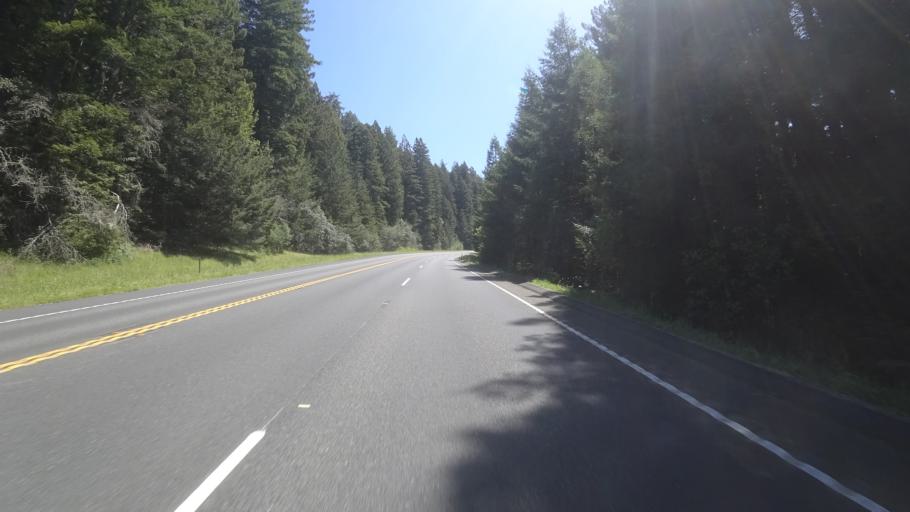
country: US
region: California
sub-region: Humboldt County
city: Blue Lake
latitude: 40.8870
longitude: -123.9736
